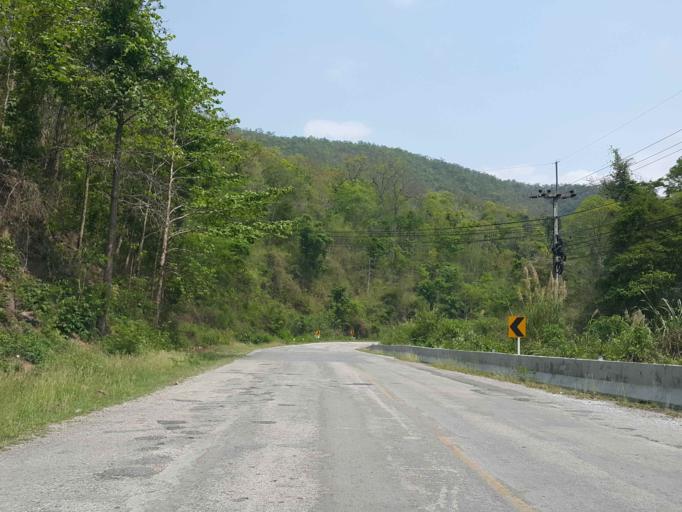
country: TH
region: Lampang
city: Thoen
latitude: 17.6379
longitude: 99.3091
